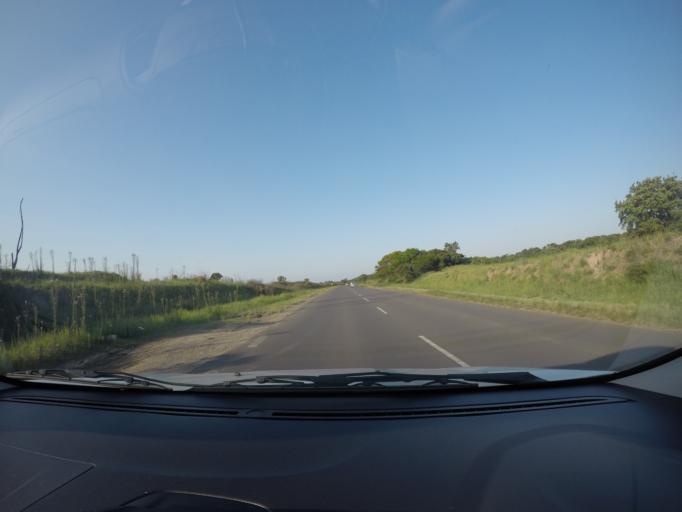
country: ZA
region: KwaZulu-Natal
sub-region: uThungulu District Municipality
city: Richards Bay
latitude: -28.7503
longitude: 32.0109
